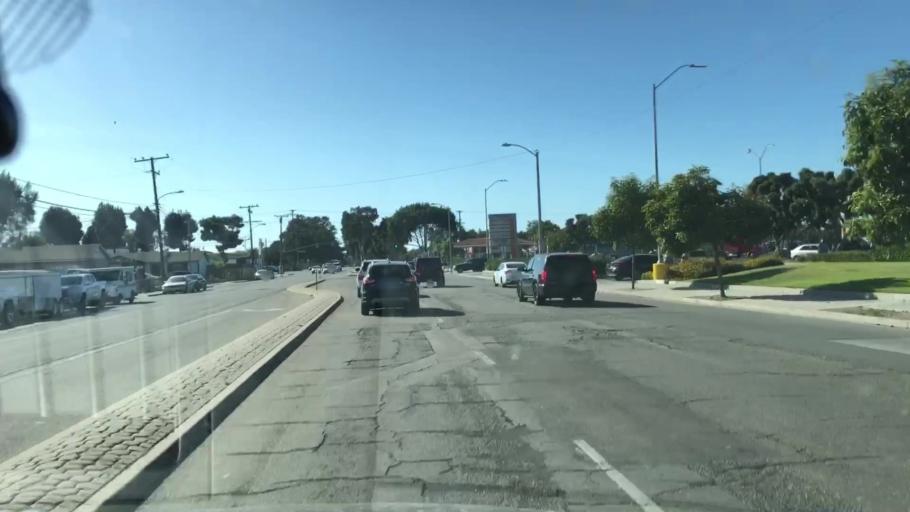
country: US
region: California
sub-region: Ventura County
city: Oxnard
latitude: 34.1757
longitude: -119.1926
